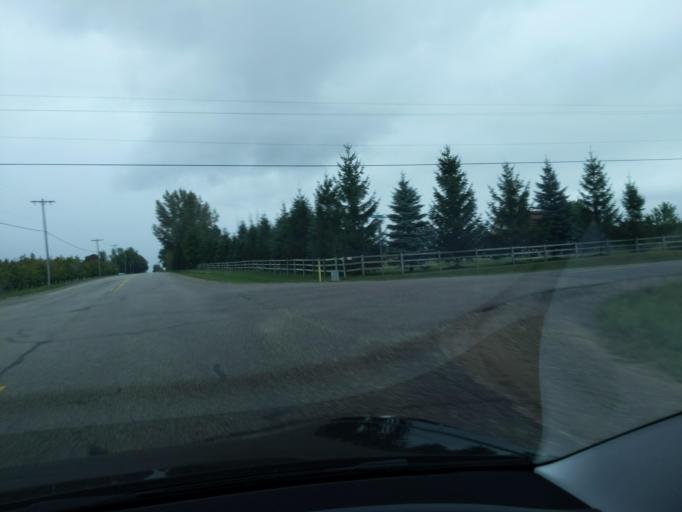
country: US
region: Michigan
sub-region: Antrim County
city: Elk Rapids
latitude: 44.8308
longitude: -85.4052
